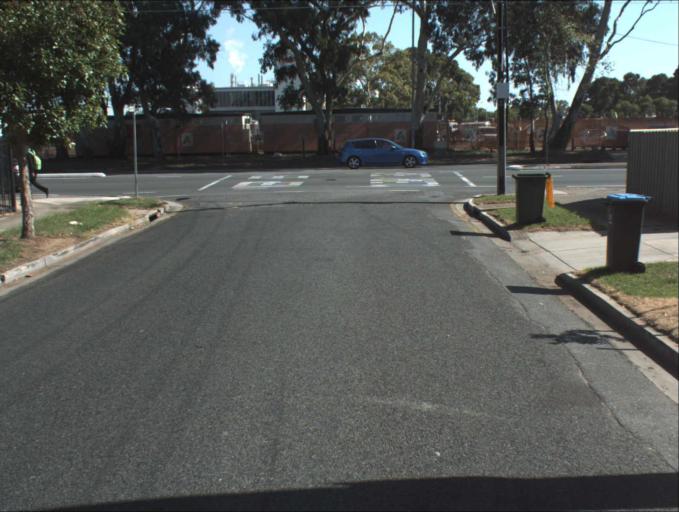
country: AU
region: South Australia
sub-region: Prospect
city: Prospect
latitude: -34.8753
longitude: 138.5747
